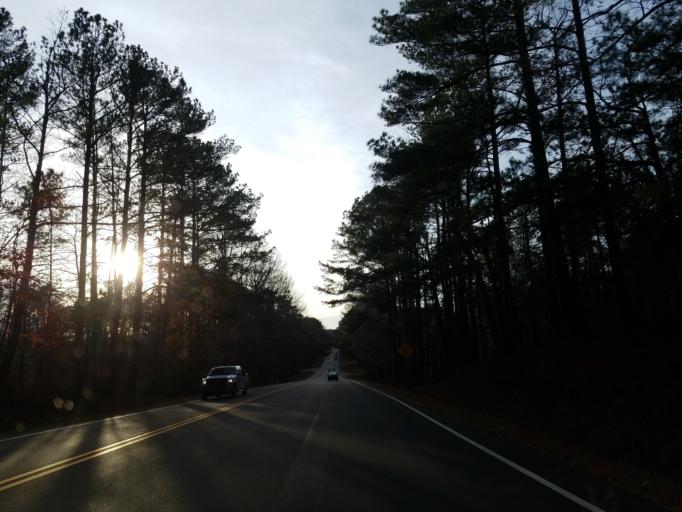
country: US
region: Georgia
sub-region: Carroll County
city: Temple
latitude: 33.7239
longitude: -85.0851
